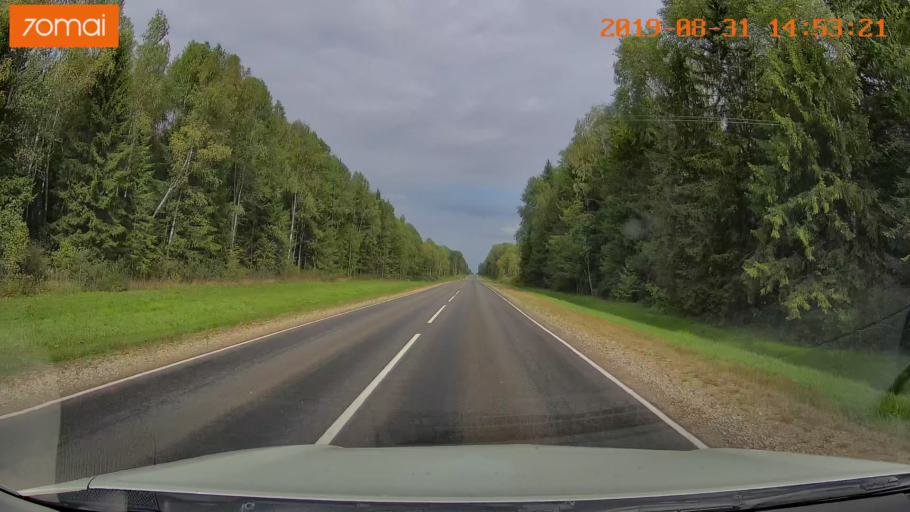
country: RU
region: Kaluga
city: Spas-Demensk
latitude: 54.2826
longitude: 33.8622
